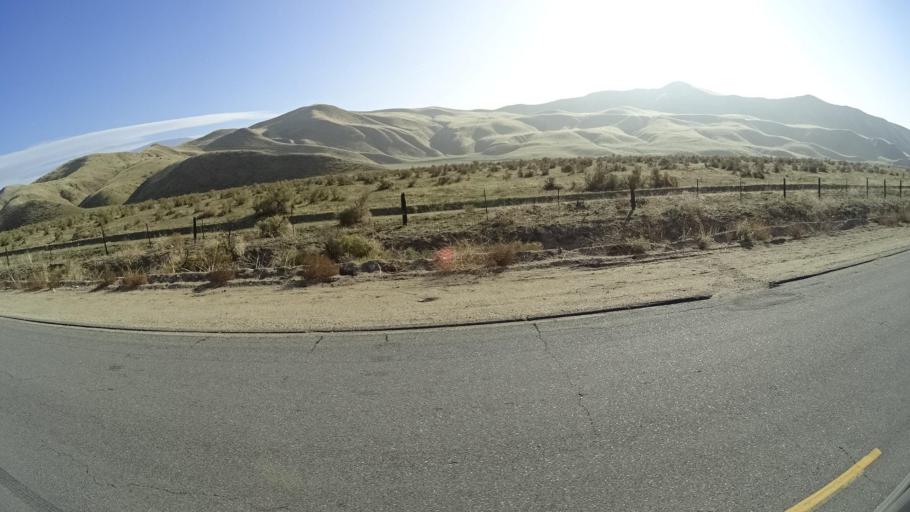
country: US
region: California
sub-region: Kern County
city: Arvin
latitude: 35.3246
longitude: -118.7234
